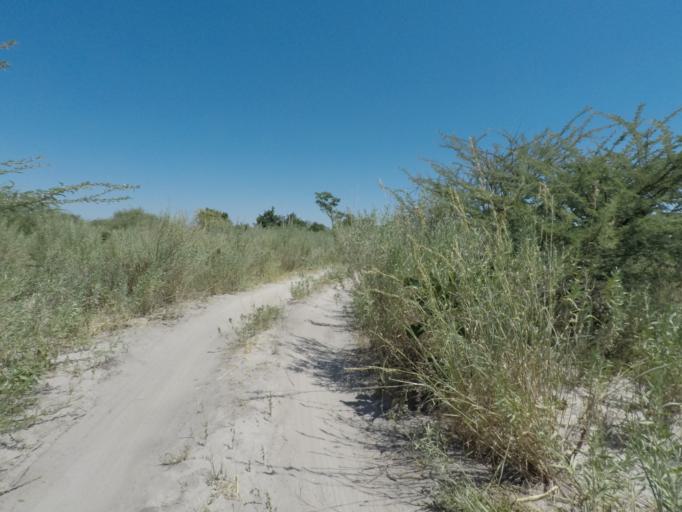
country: BW
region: North West
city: Maun
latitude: -19.4730
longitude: 23.5545
